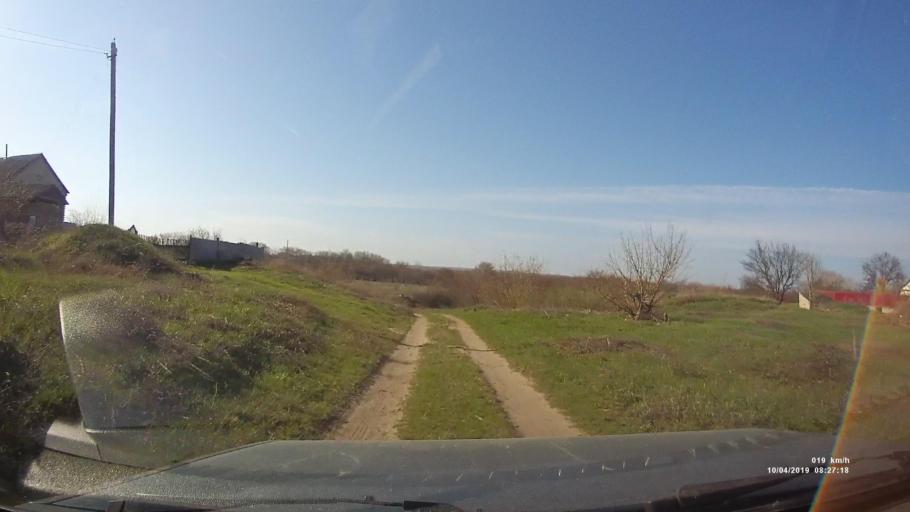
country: RU
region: Rostov
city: Kamensk-Shakhtinskiy
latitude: 48.3573
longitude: 40.2245
